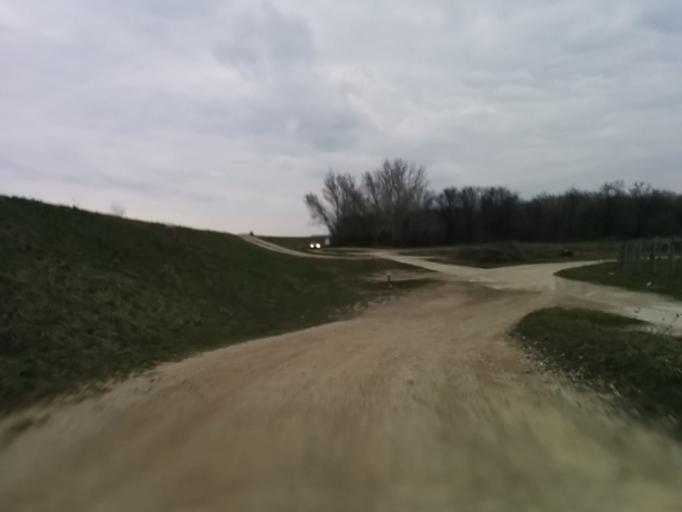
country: SK
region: Trnavsky
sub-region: Okres Galanta
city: Galanta
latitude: 48.2325
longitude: 17.8148
